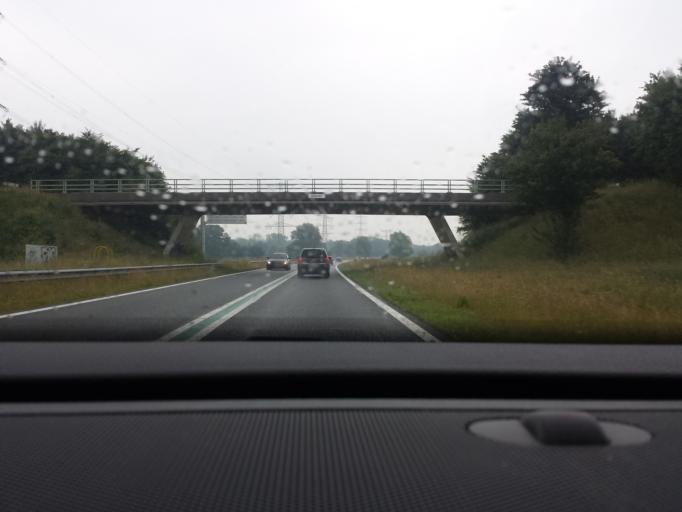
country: NL
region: Overijssel
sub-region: Gemeente Enschede
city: Enschede
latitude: 52.2027
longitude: 6.9109
